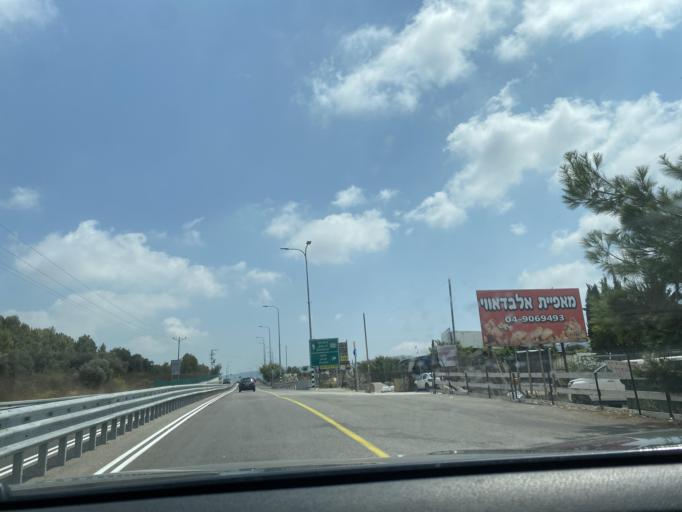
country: IL
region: Northern District
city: Kefar Weradim
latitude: 33.0020
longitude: 35.2978
